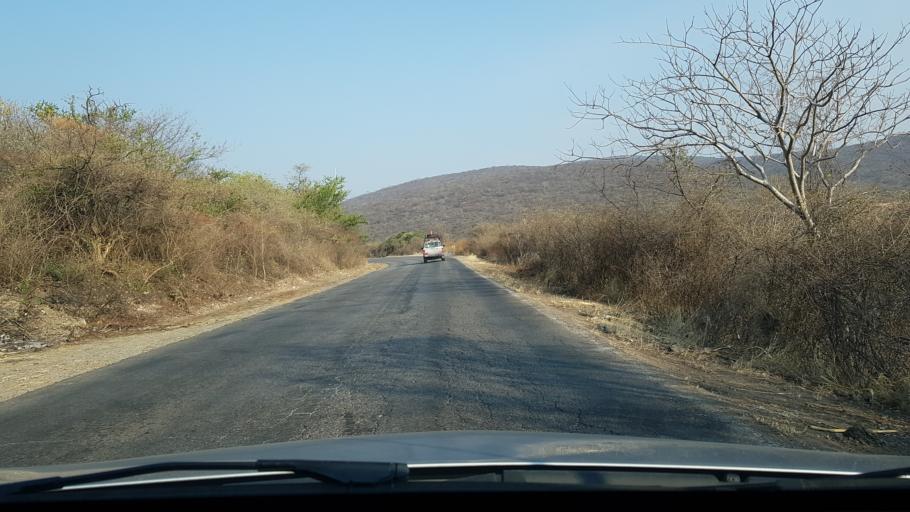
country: MX
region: Morelos
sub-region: Tlaltizapan de Zapata
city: Colonia Palo Prieto (Chipitongo)
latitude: 18.6744
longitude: -99.0609
